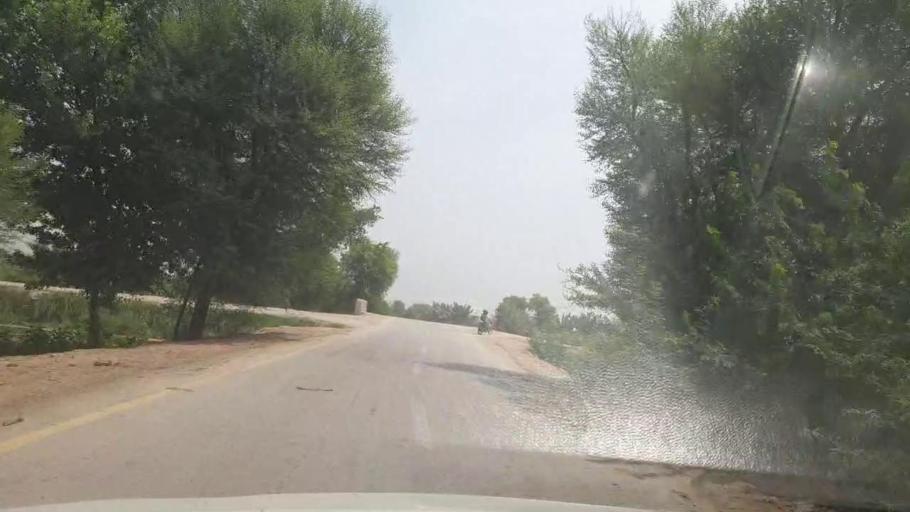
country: PK
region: Sindh
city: Kot Diji
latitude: 27.3743
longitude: 68.6513
